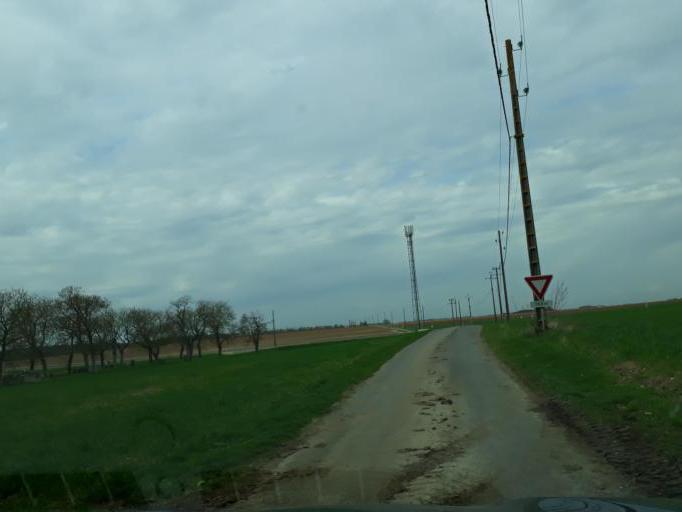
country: FR
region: Centre
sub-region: Departement du Loiret
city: Epieds-en-Beauce
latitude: 47.9350
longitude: 1.6084
